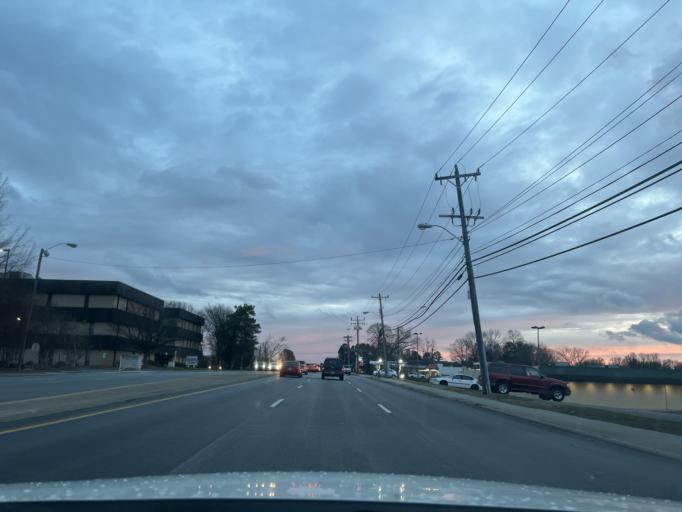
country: US
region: North Carolina
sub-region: Guilford County
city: Greensboro
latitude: 36.0389
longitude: -79.8499
